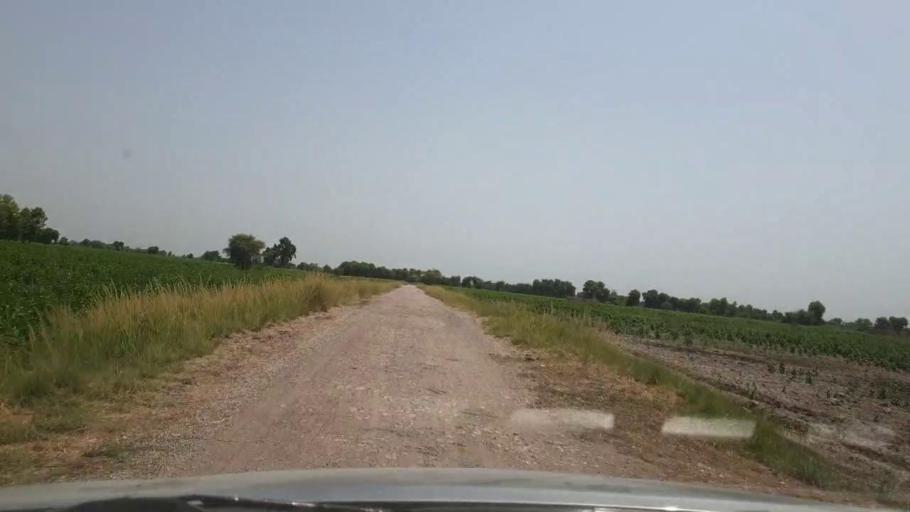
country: PK
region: Sindh
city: Pano Aqil
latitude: 27.8011
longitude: 69.2419
